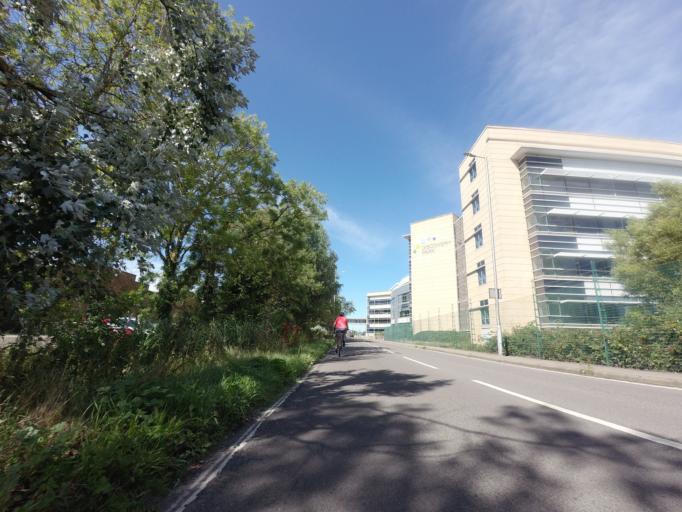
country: GB
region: England
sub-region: Kent
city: Sandwich
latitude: 51.2854
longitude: 1.3455
